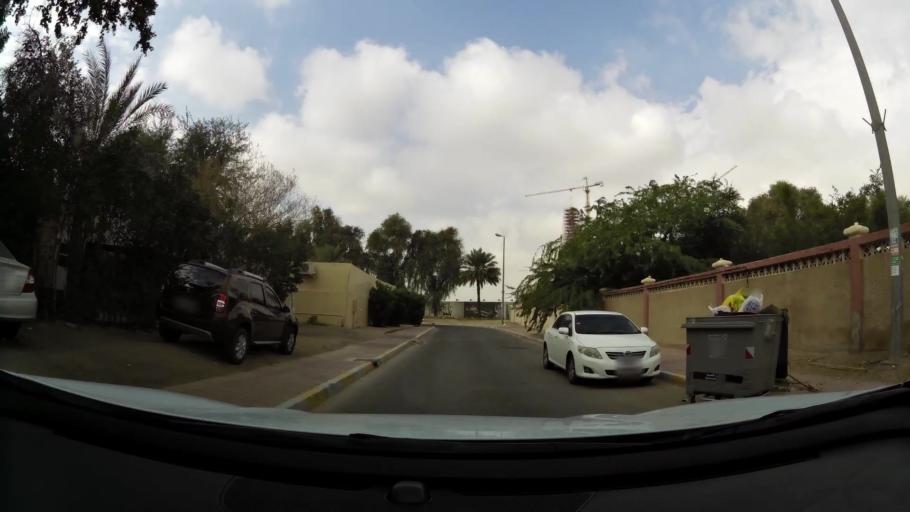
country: AE
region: Abu Dhabi
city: Al Ain
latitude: 24.2256
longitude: 55.7519
